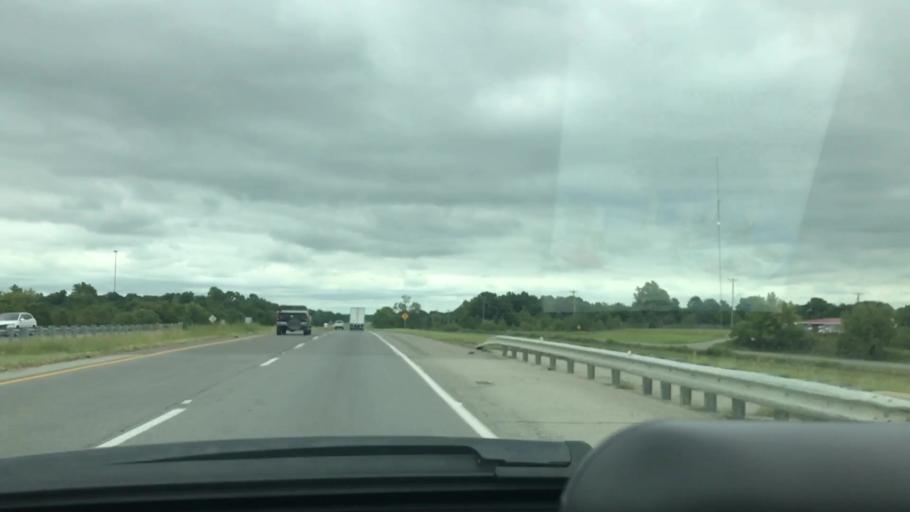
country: US
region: Oklahoma
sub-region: McIntosh County
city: Eufaula
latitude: 35.3625
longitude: -95.5740
